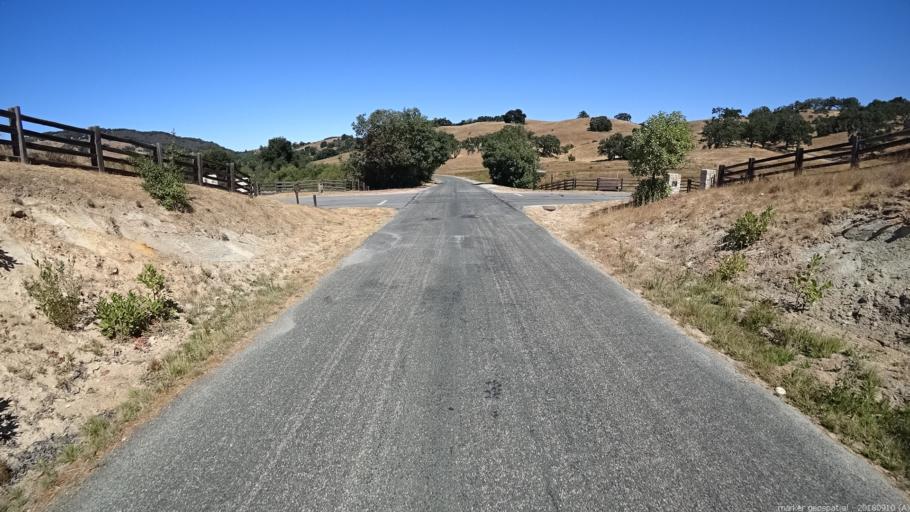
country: US
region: California
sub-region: Monterey County
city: Carmel Valley Village
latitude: 36.4540
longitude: -121.7970
